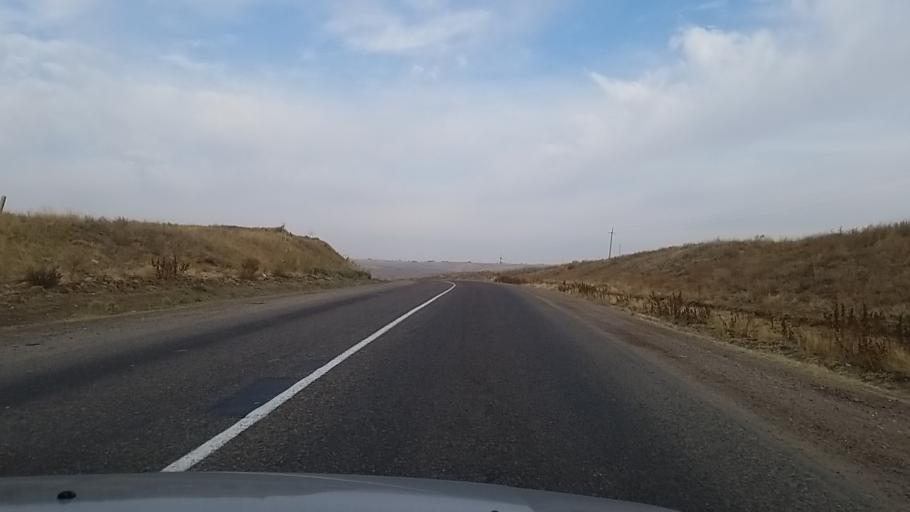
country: KZ
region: Almaty Oblysy
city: Burunday
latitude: 43.4947
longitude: 76.6626
